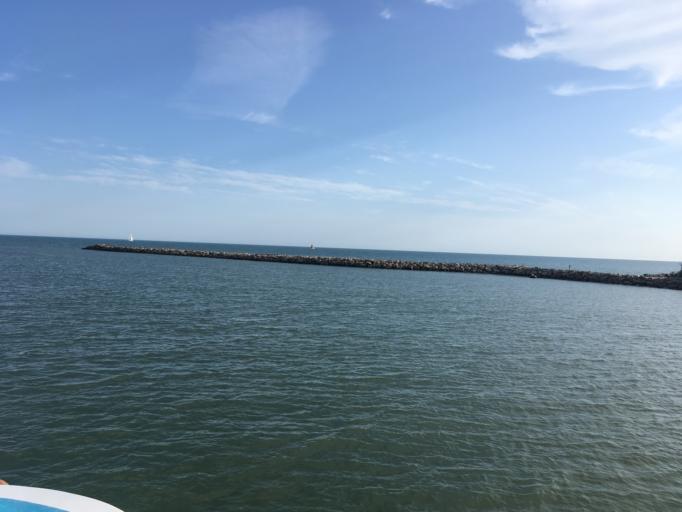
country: FR
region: Provence-Alpes-Cote d'Azur
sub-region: Departement des Bouches-du-Rhone
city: Saintes-Maries-de-la-Mer
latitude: 43.4518
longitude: 4.3964
